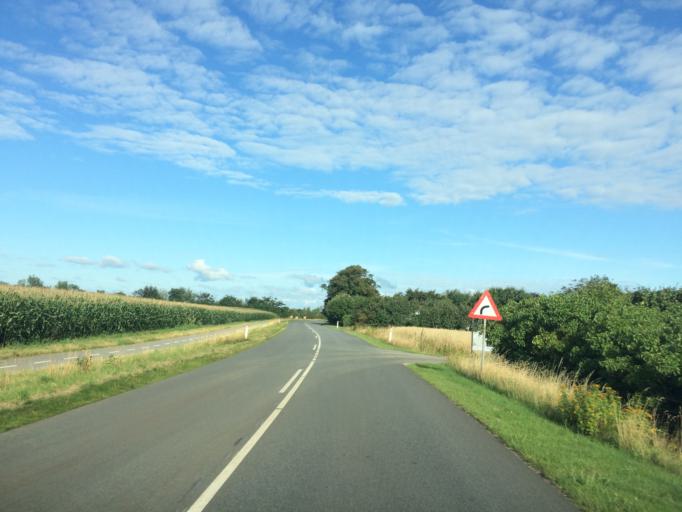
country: DK
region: South Denmark
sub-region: Varde Kommune
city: Oksbol
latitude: 55.8429
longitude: 8.3019
